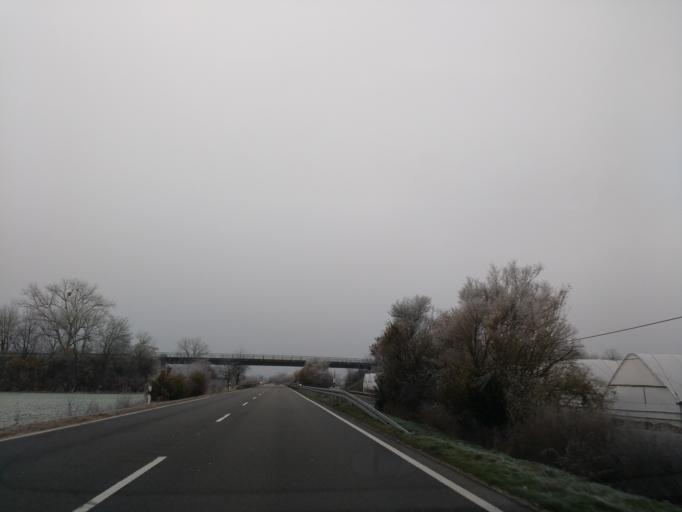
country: DE
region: Baden-Wuerttemberg
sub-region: Freiburg Region
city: Haslach
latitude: 48.5395
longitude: 8.0370
